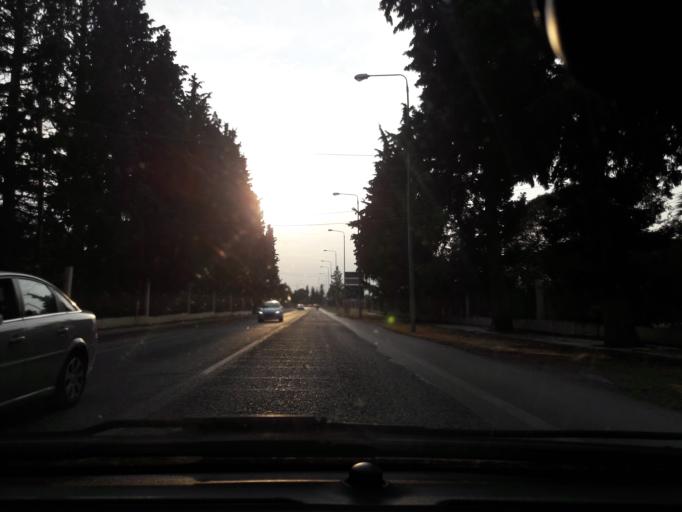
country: GR
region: Central Macedonia
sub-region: Nomos Thessalonikis
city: Thermi
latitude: 40.5390
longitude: 22.9952
